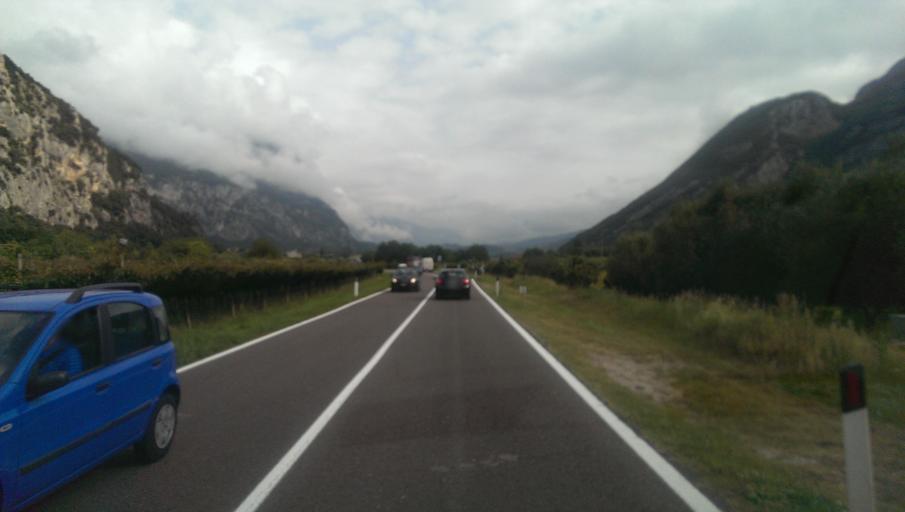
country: IT
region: Trentino-Alto Adige
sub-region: Provincia di Trento
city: Arco
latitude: 45.9379
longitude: 10.9002
